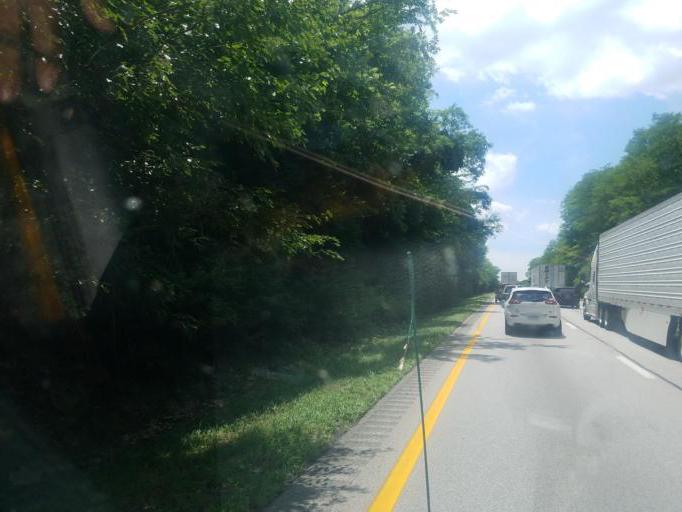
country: US
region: Kentucky
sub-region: Oldham County
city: Orchard Grass Hills
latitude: 38.3349
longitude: -85.5317
